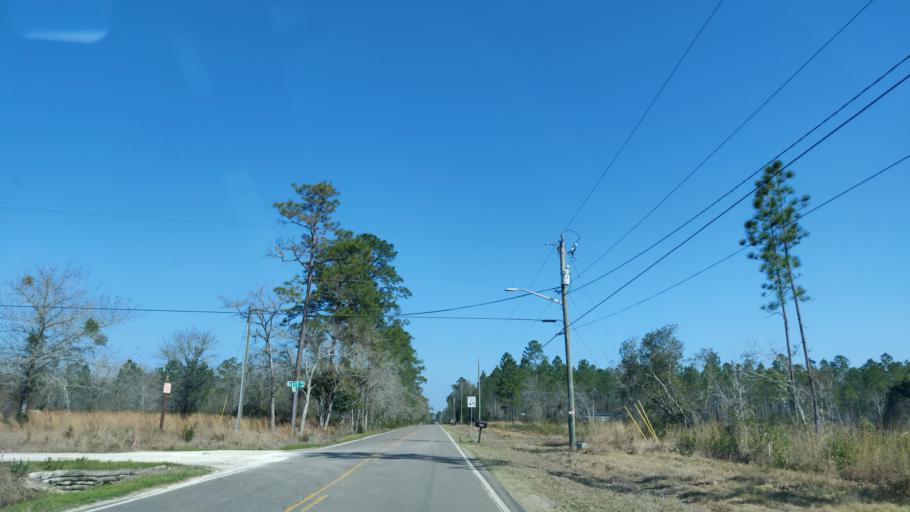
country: US
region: Florida
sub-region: Duval County
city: Baldwin
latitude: 30.1943
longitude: -81.9660
